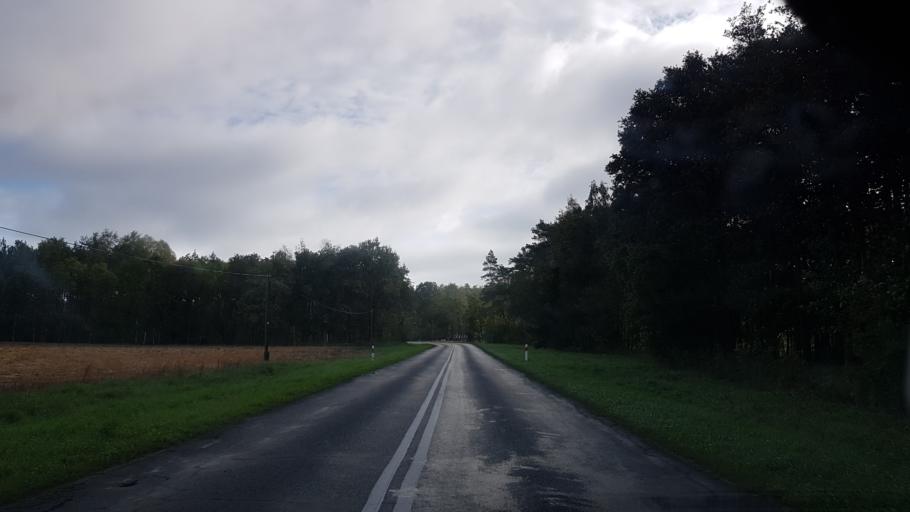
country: PL
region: Greater Poland Voivodeship
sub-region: Leszno
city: Leszno
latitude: 51.7862
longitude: 16.5510
